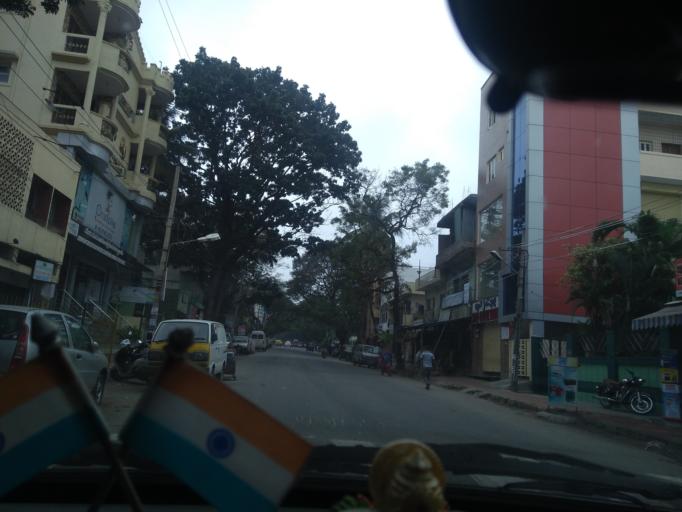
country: IN
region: Karnataka
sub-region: Bangalore Urban
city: Bangalore
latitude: 12.9898
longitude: 77.5559
